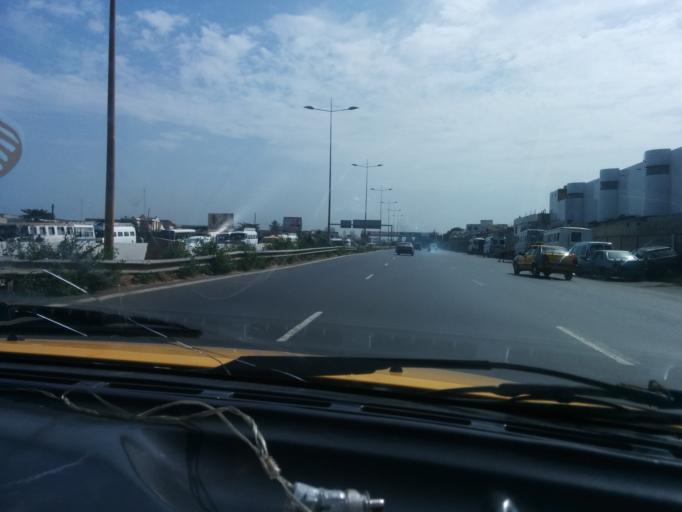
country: SN
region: Dakar
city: Dakar
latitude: 14.6964
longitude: -17.4425
